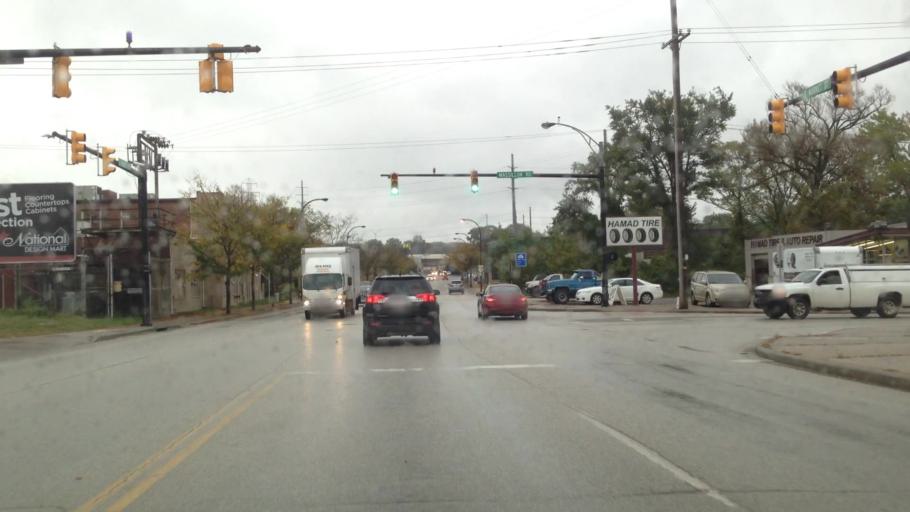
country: US
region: Ohio
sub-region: Summit County
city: Sawyerwood
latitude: 41.0620
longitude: -81.4630
